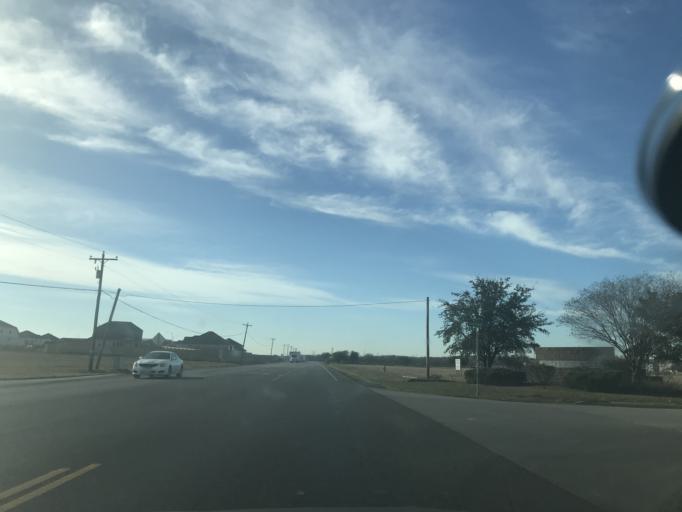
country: US
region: Texas
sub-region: Travis County
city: Manor
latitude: 30.3355
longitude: -97.5591
